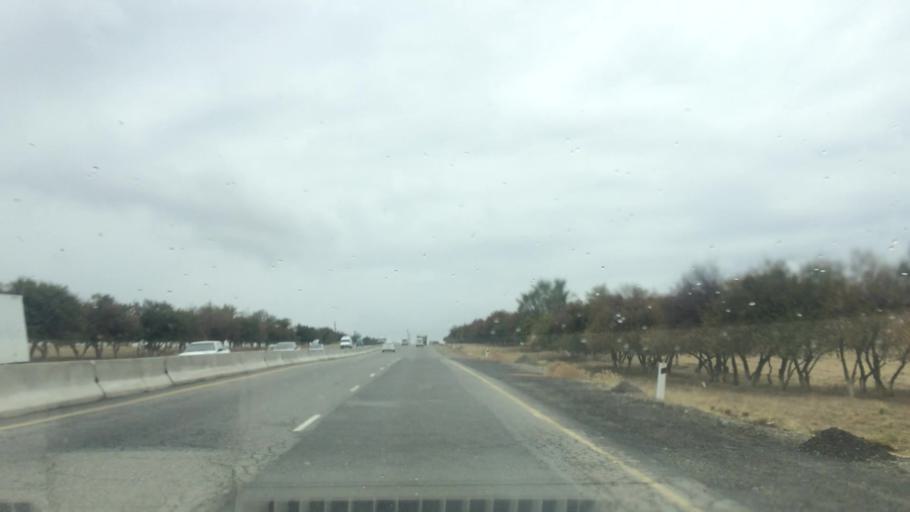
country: UZ
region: Samarqand
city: Bulung'ur
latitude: 39.8577
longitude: 67.4680
